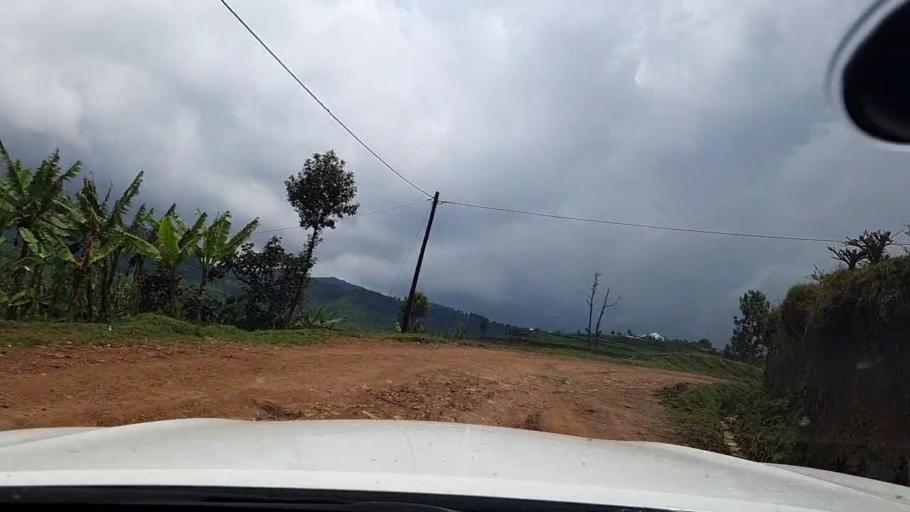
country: RW
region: Western Province
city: Kibuye
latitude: -2.1712
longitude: 29.4337
